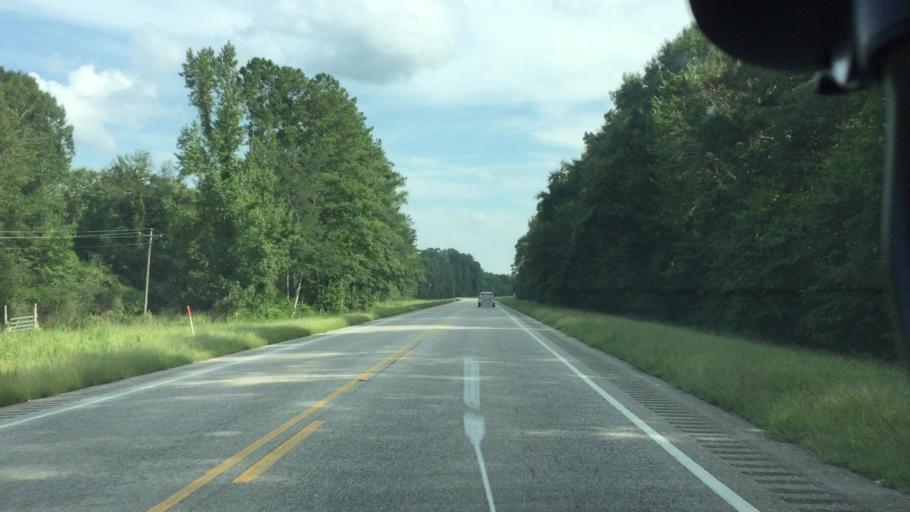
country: US
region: Alabama
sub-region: Pike County
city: Brundidge
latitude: 31.6394
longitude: -85.9467
